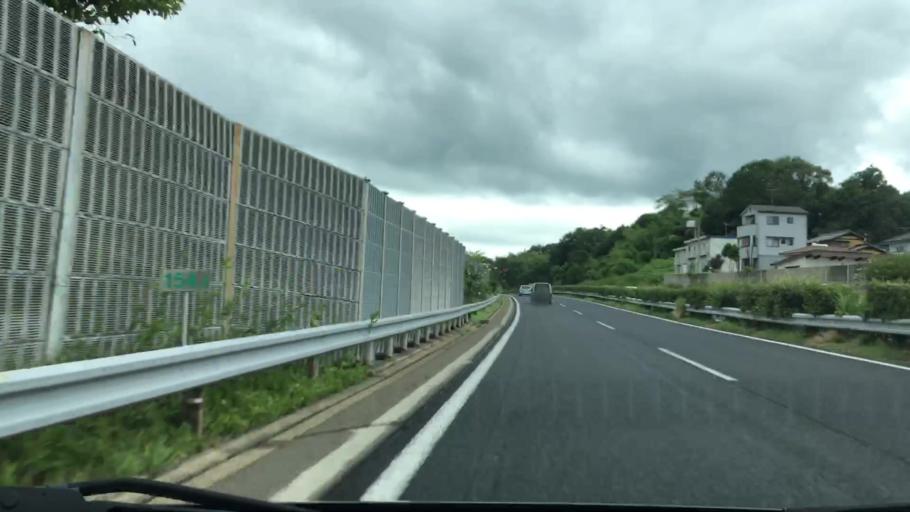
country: JP
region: Okayama
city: Tsuyama
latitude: 35.0763
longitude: 134.0176
